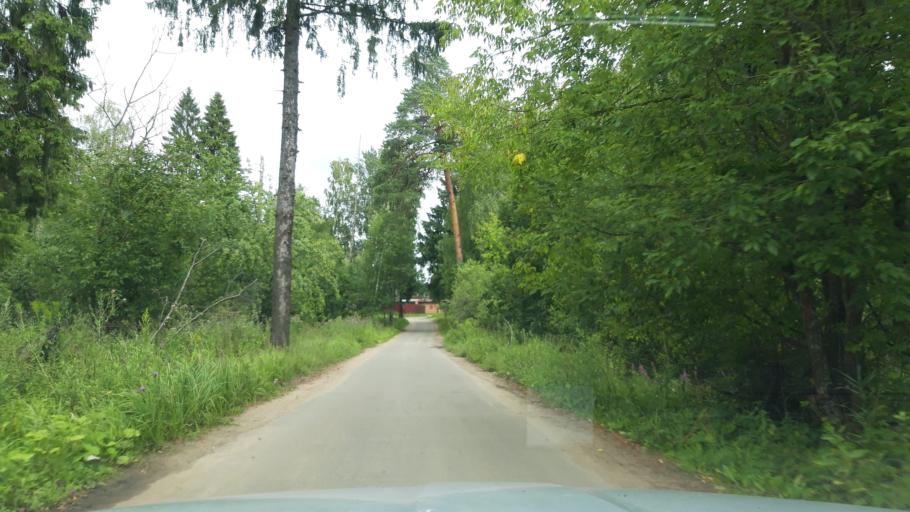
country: RU
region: Moskovskaya
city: Povarovo
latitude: 56.0612
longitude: 37.0730
